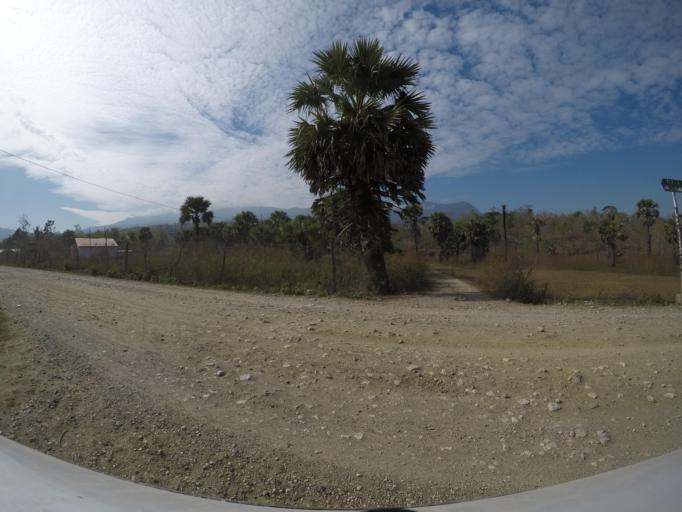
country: TL
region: Bobonaro
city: Maliana
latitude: -8.9944
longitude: 125.2036
